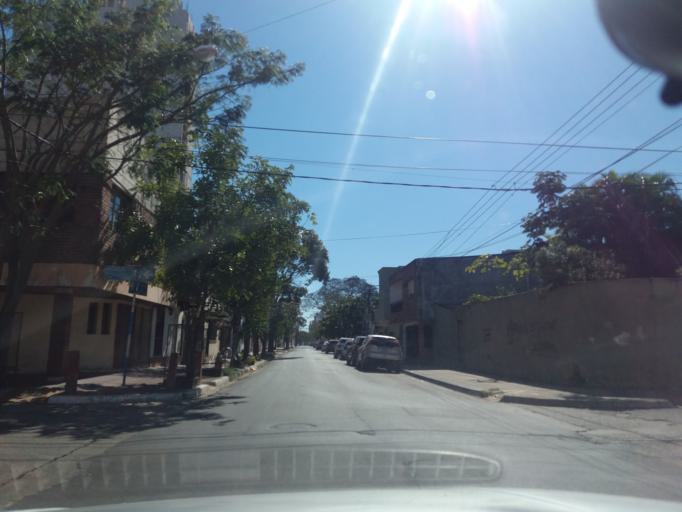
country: AR
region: Corrientes
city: Corrientes
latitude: -27.4740
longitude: -58.8411
